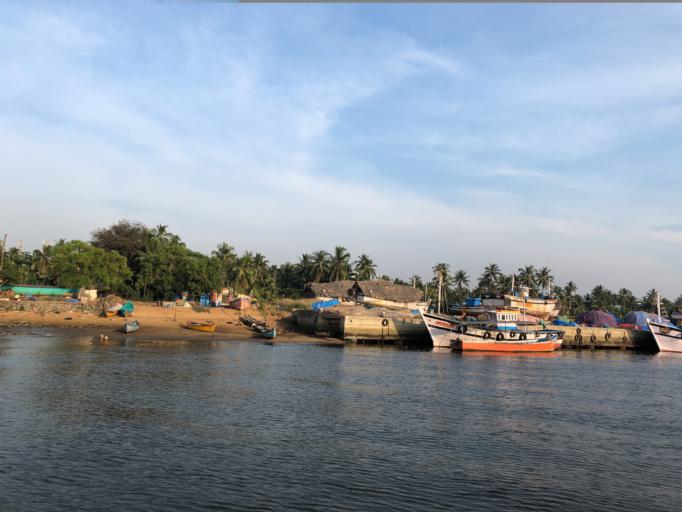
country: IN
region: Karnataka
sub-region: Dakshina Kannada
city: Mangalore
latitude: 12.8878
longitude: 74.8198
